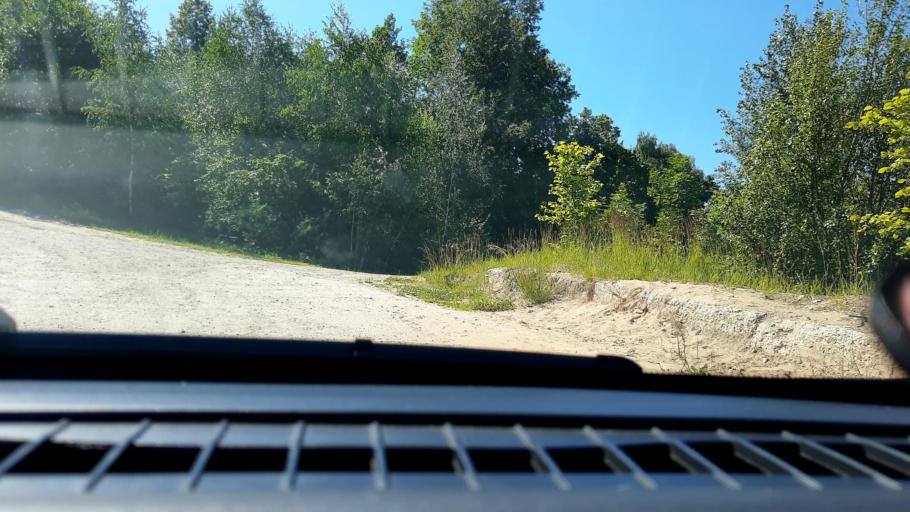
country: RU
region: Nizjnij Novgorod
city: Nizhniy Novgorod
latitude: 56.2287
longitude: 43.9192
